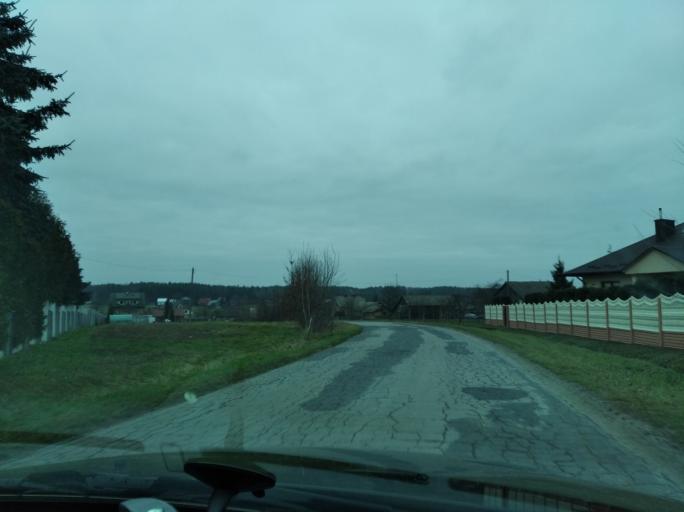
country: PL
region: Subcarpathian Voivodeship
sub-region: Powiat lancucki
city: Brzoza Stadnicka
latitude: 50.1892
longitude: 22.2570
